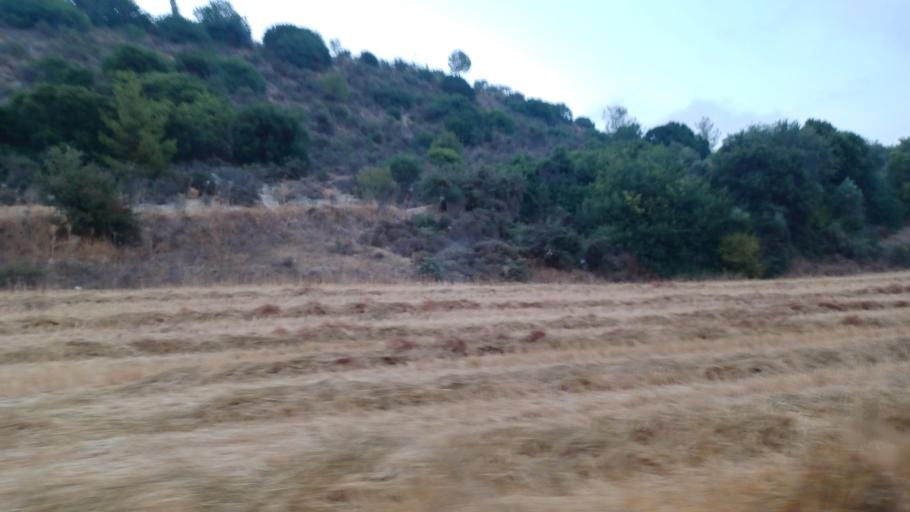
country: CY
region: Pafos
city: Mesogi
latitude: 34.8100
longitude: 32.5741
